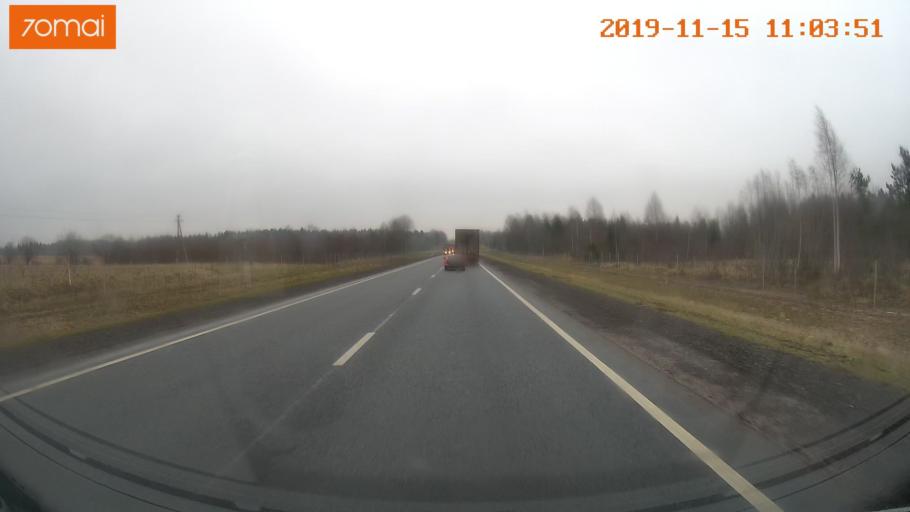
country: RU
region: Vologda
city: Chebsara
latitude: 59.1227
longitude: 38.9714
